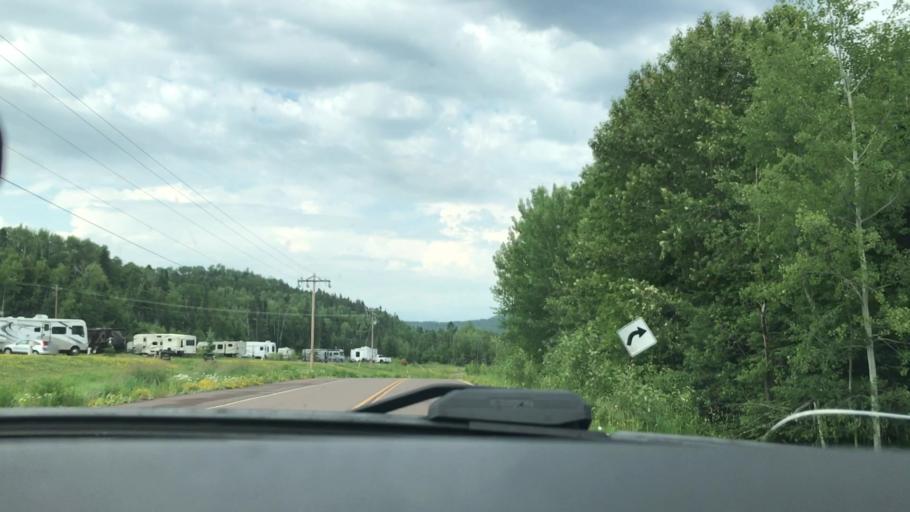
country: CA
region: Ontario
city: Neebing
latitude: 47.9549
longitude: -89.6925
